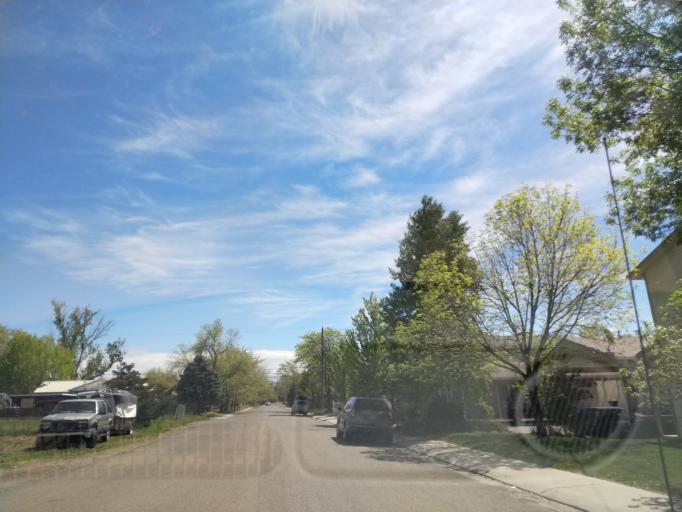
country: US
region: Colorado
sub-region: Mesa County
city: Grand Junction
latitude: 39.0801
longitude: -108.5749
